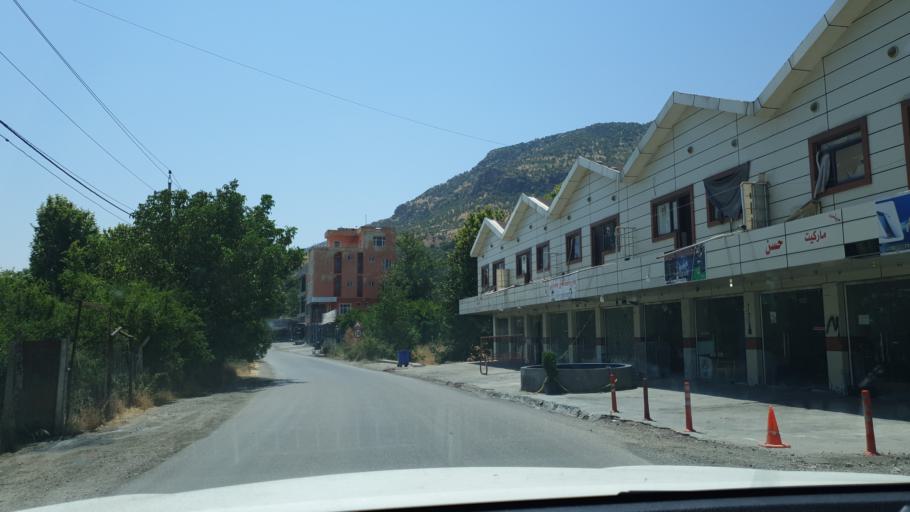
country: IQ
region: Arbil
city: Nahiyat Hiran
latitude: 36.2811
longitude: 44.4947
